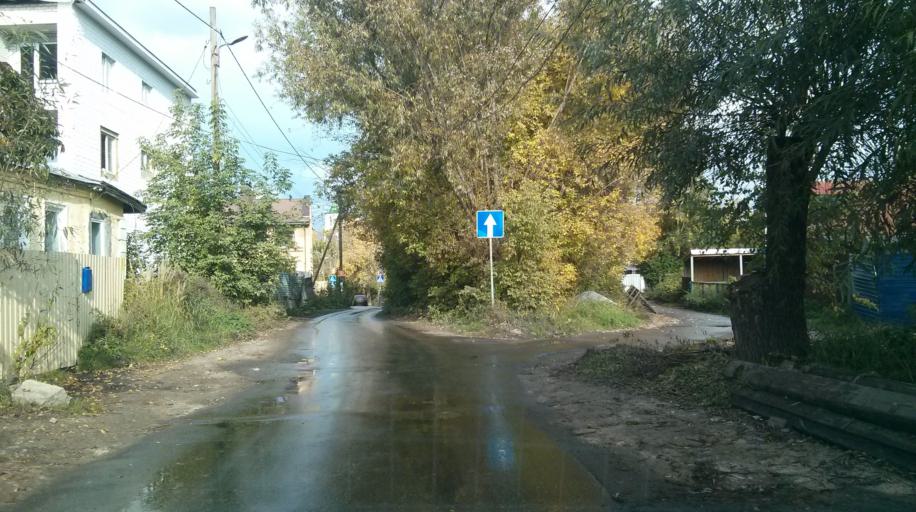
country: RU
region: Nizjnij Novgorod
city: Nizhniy Novgorod
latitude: 56.3058
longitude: 44.0431
